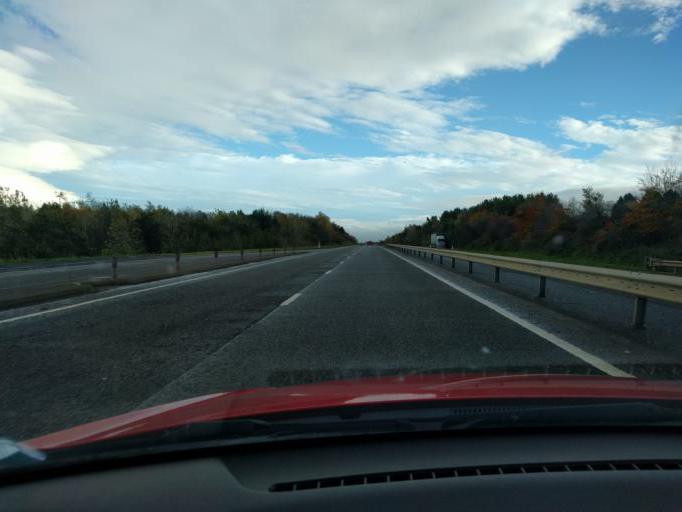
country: GB
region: Scotland
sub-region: East Lothian
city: Dunbar
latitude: 55.9751
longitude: -2.4739
